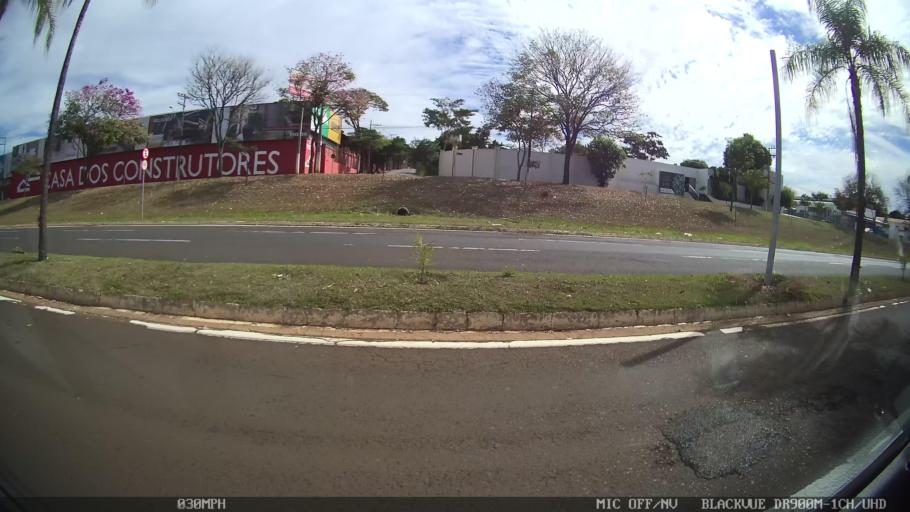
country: BR
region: Sao Paulo
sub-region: Catanduva
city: Catanduva
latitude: -21.1537
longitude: -48.9819
